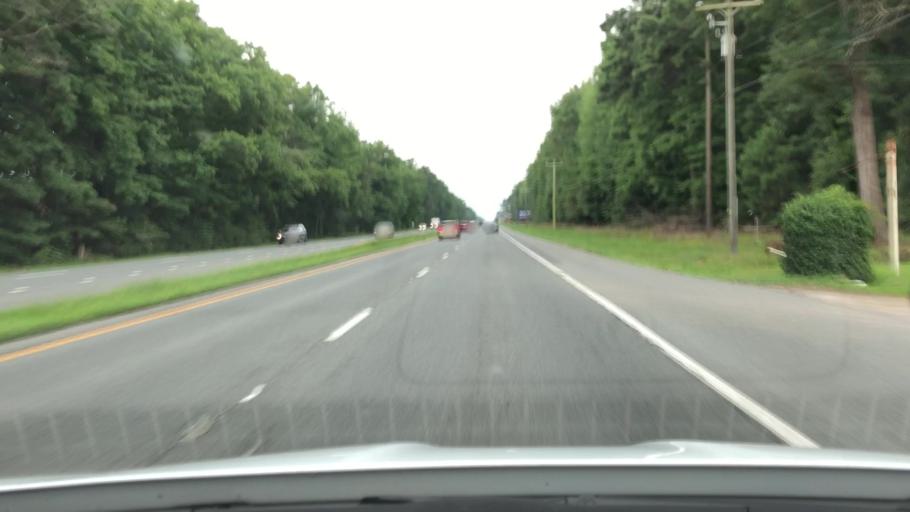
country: US
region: Virginia
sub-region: Northampton County
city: Cape Charles
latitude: 37.2023
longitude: -75.9669
